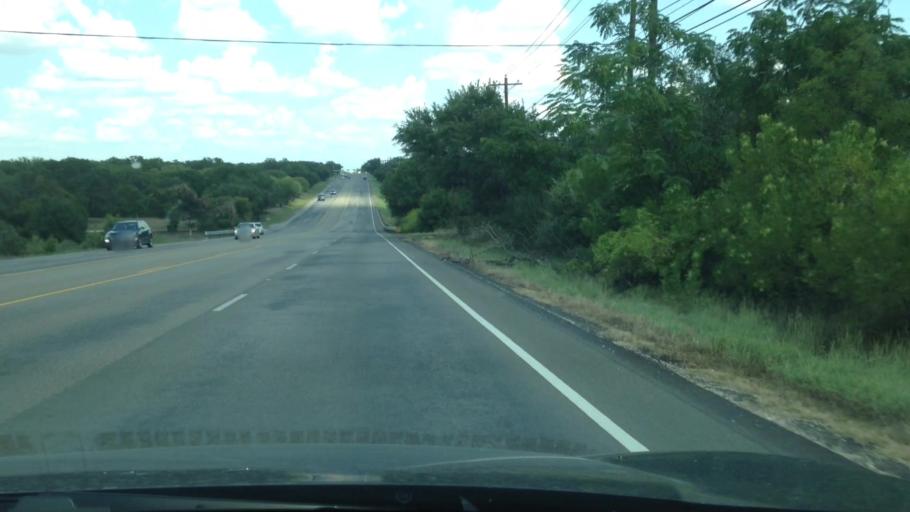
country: US
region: Texas
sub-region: Williamson County
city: Georgetown
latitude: 30.6334
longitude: -97.7715
